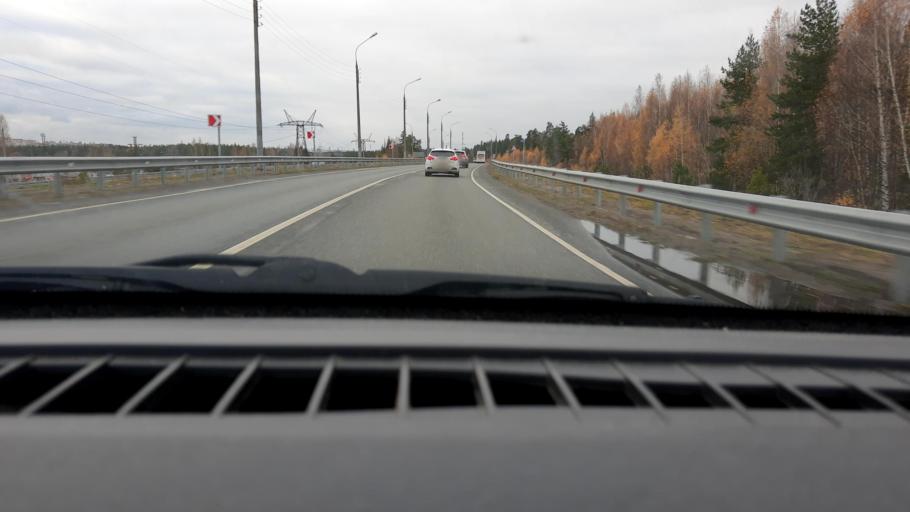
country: RU
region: Nizjnij Novgorod
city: Kstovo
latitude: 56.1779
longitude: 44.1544
